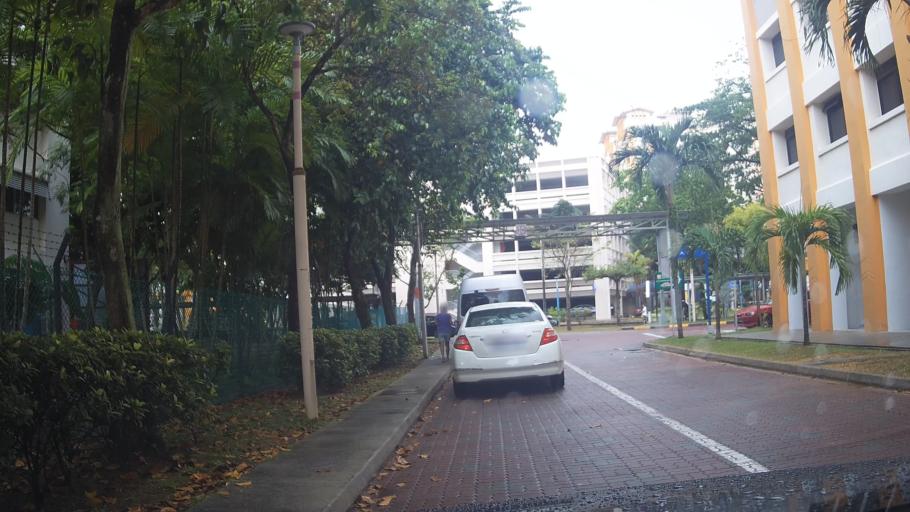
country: MY
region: Johor
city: Johor Bahru
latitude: 1.4426
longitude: 103.8002
